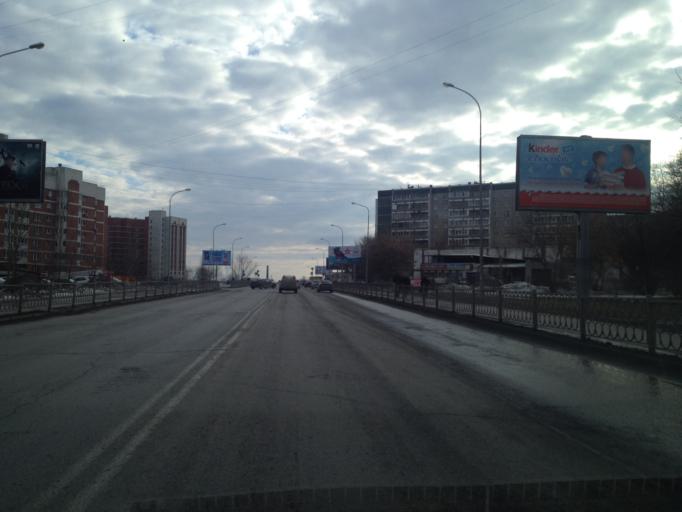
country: RU
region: Sverdlovsk
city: Yekaterinburg
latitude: 56.8513
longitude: 60.5695
